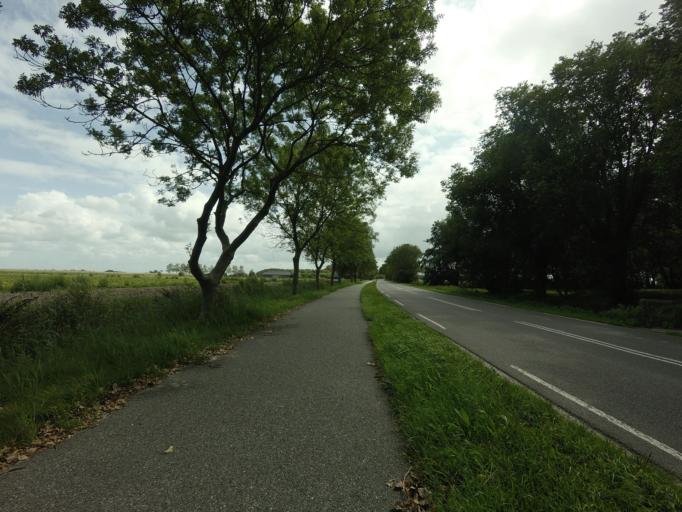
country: NL
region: Friesland
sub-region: Gemeente Harlingen
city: Harlingen
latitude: 53.1356
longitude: 5.4652
